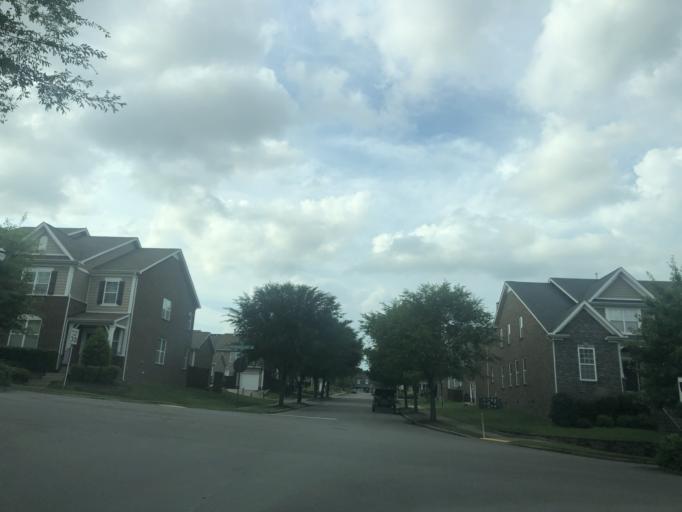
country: US
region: Tennessee
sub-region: Davidson County
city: Lakewood
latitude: 36.1681
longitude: -86.6191
